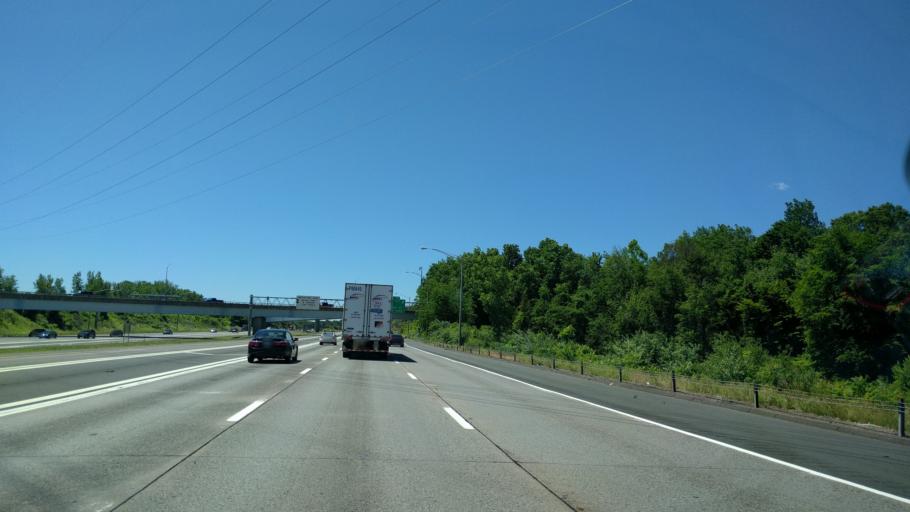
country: US
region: Connecticut
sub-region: Hartford County
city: Manchester
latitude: 41.7899
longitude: -72.5639
